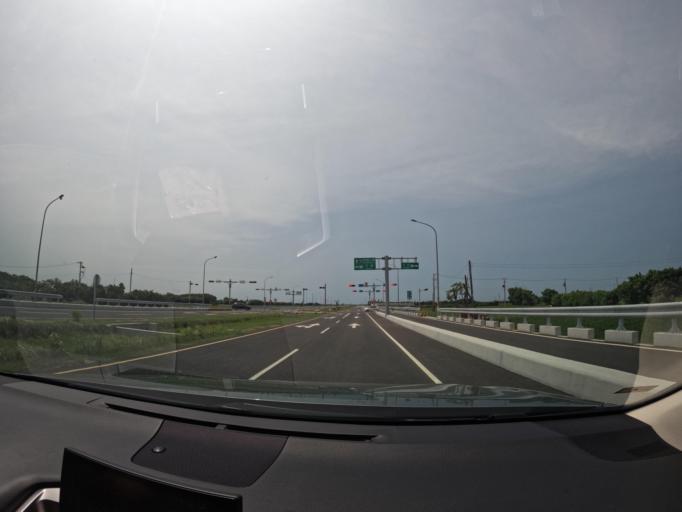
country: TW
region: Taiwan
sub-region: Changhua
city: Chang-hua
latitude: 23.9378
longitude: 120.3457
